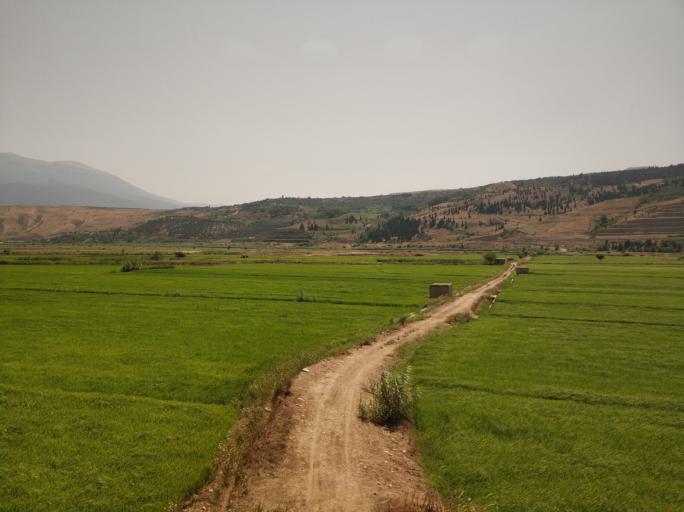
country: IR
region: Gilan
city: Pa'in-e Bazar-e Rudbar
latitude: 36.8726
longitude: 49.4928
